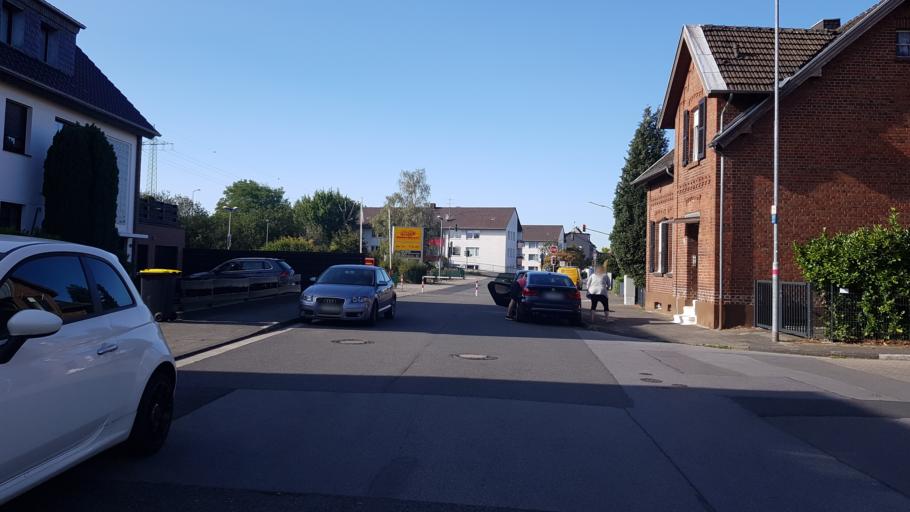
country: DE
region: North Rhine-Westphalia
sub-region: Regierungsbezirk Dusseldorf
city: Ratingen
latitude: 51.3439
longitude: 6.8256
